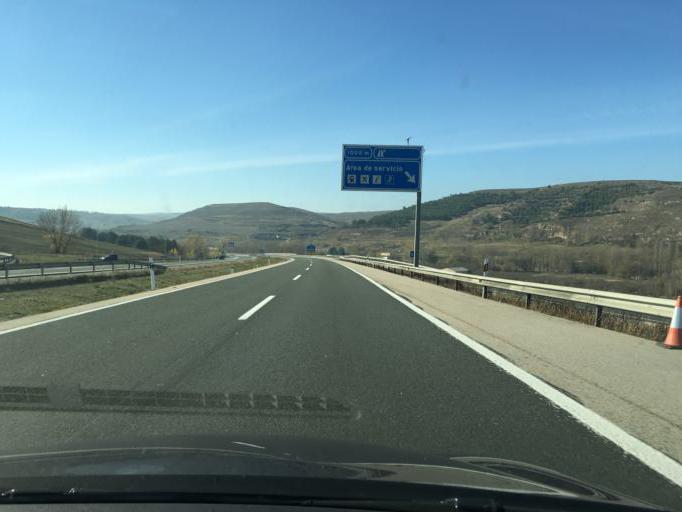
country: ES
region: Castille and Leon
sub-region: Provincia de Burgos
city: Briviesca
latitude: 42.5321
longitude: -3.3203
